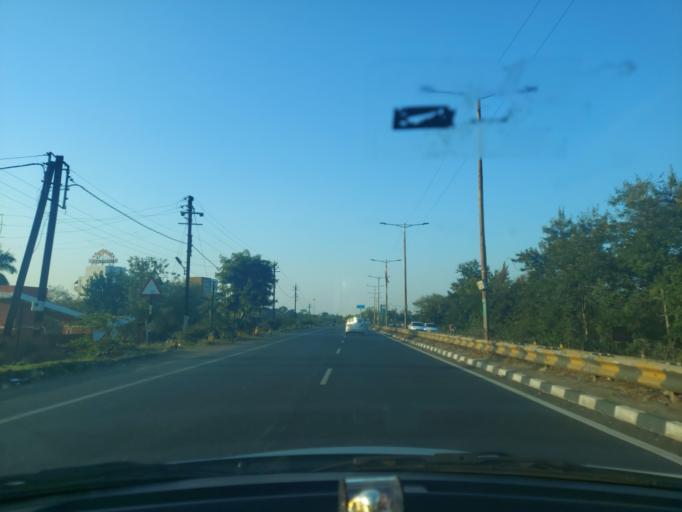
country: IN
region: Madhya Pradesh
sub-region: Ujjain
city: Ujjain
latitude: 23.1244
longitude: 75.7961
